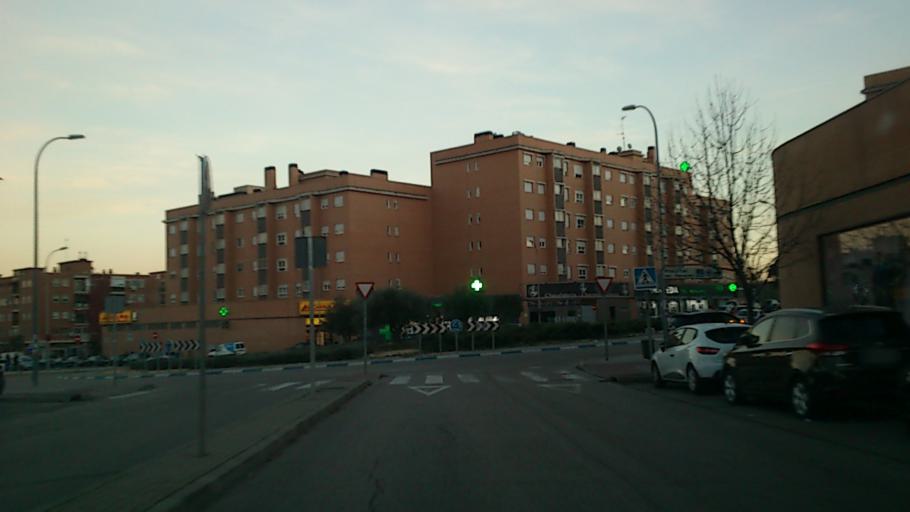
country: ES
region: Madrid
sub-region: Provincia de Madrid
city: San Fernando de Henares
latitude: 40.4226
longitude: -3.5357
